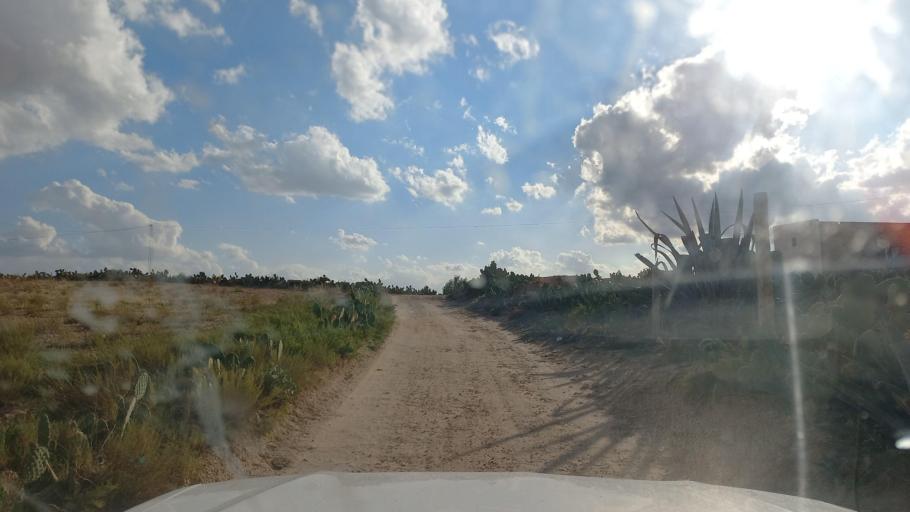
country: TN
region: Al Qasrayn
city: Sbiba
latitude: 35.3763
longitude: 9.0722
